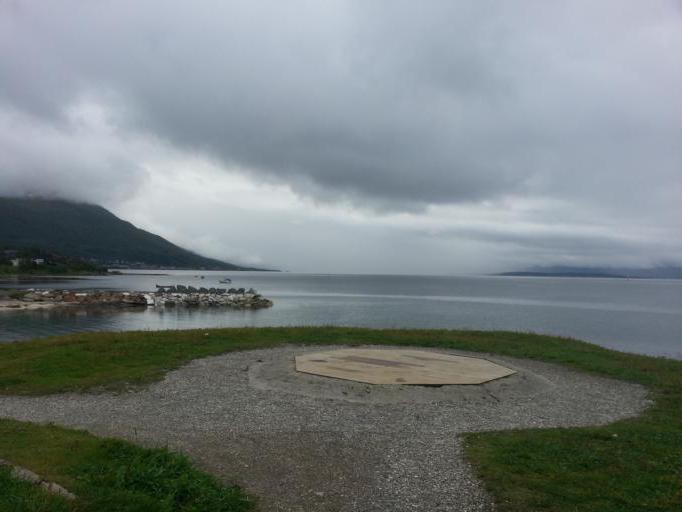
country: NO
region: Troms
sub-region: Tromso
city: Tromso
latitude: 69.6324
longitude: 18.9054
